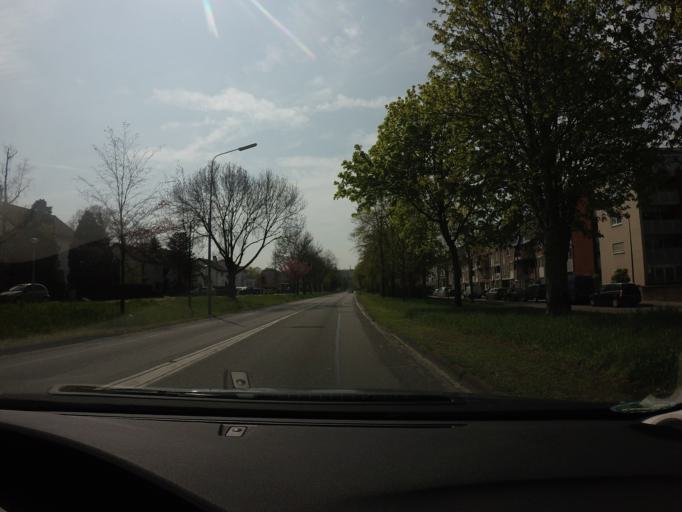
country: NL
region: Limburg
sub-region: Gemeente Maastricht
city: Maastricht
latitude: 50.8387
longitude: 5.6954
